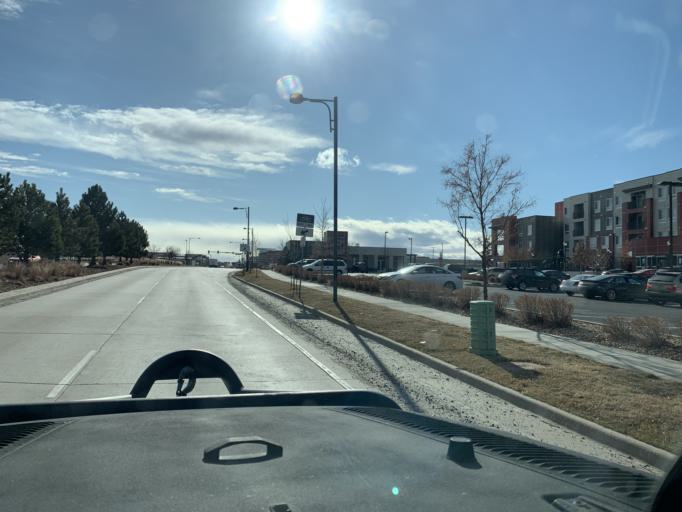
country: US
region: Colorado
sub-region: Adams County
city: Aurora
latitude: 39.7620
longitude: -104.8659
